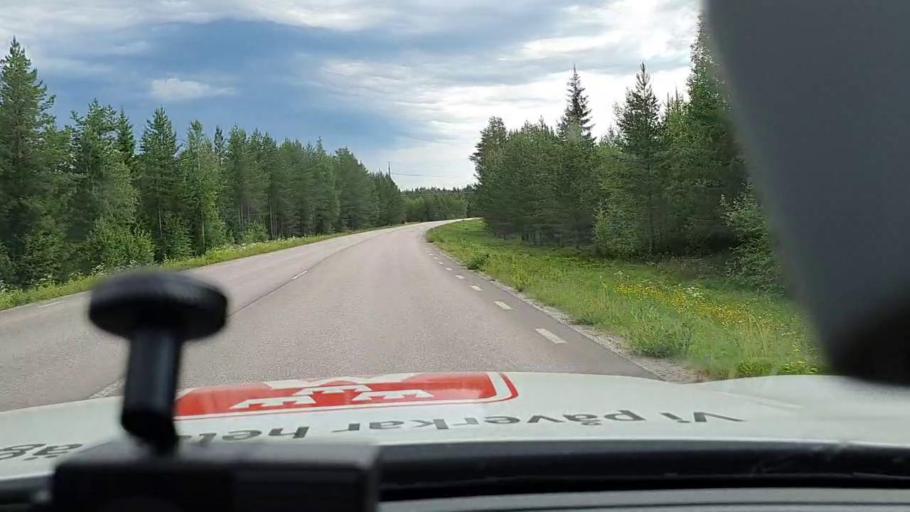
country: SE
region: Norrbotten
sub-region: Bodens Kommun
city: Boden
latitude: 65.8197
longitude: 21.5913
